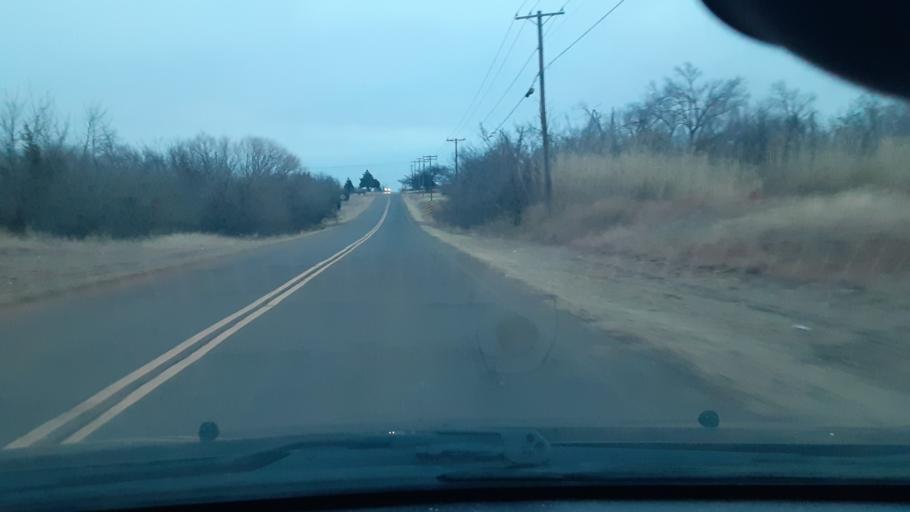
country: US
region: Oklahoma
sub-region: Logan County
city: Guthrie
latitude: 35.8562
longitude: -97.4104
